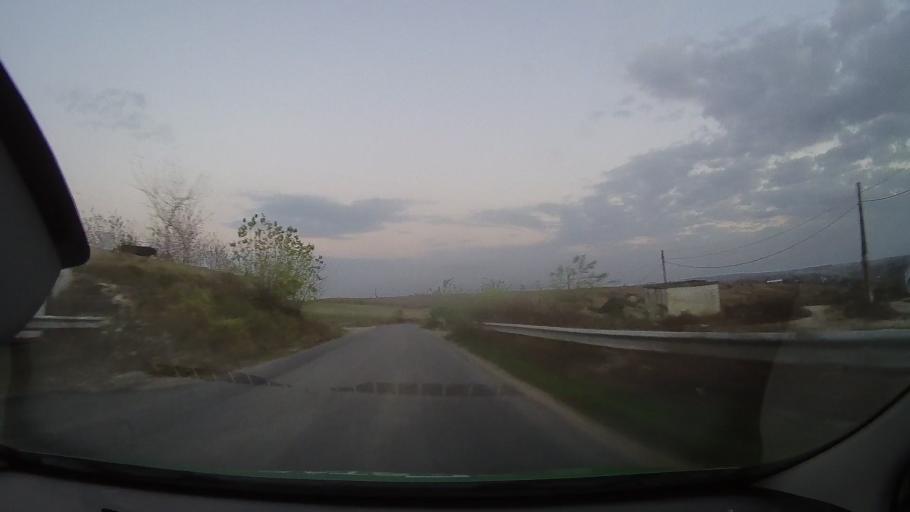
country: RO
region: Constanta
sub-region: Comuna Baneasa
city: Baneasa
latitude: 44.0786
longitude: 27.6945
